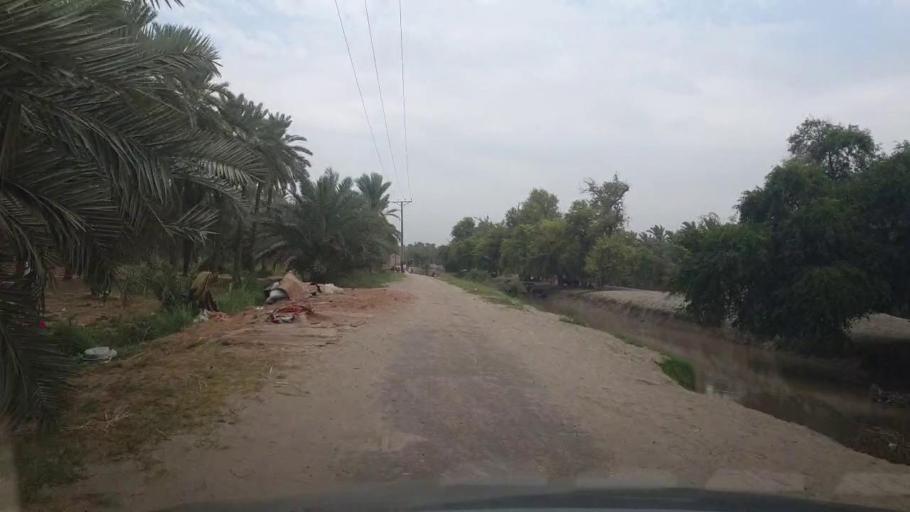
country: PK
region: Sindh
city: Khairpur
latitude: 27.6266
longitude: 68.7668
